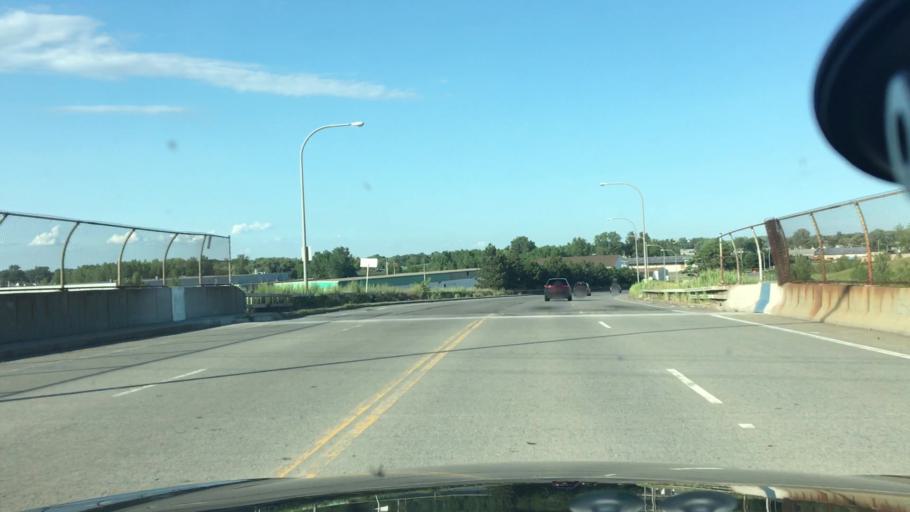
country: US
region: New York
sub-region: Erie County
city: Lackawanna
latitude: 42.8455
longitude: -78.8414
